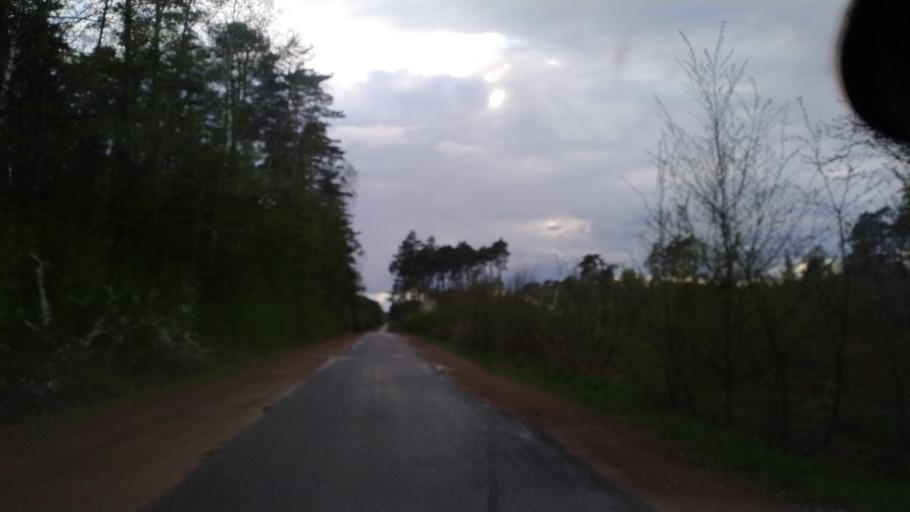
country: PL
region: Pomeranian Voivodeship
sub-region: Powiat starogardzki
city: Osiek
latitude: 53.6932
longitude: 18.5377
